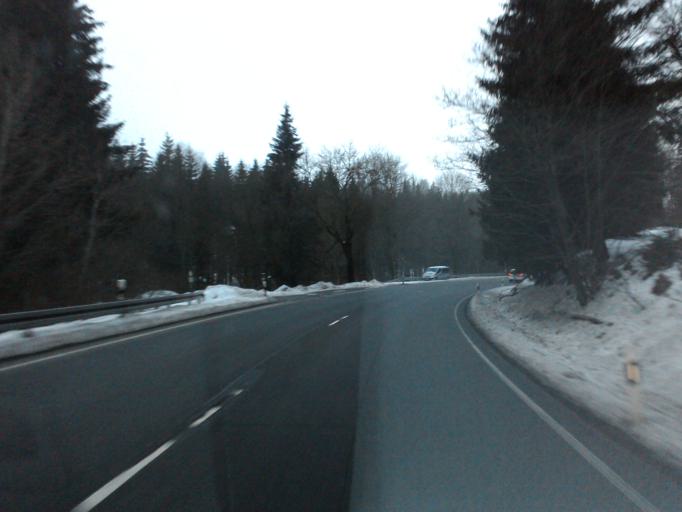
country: DE
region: North Rhine-Westphalia
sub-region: Regierungsbezirk Arnsberg
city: Winterberg
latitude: 51.2392
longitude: 8.5275
